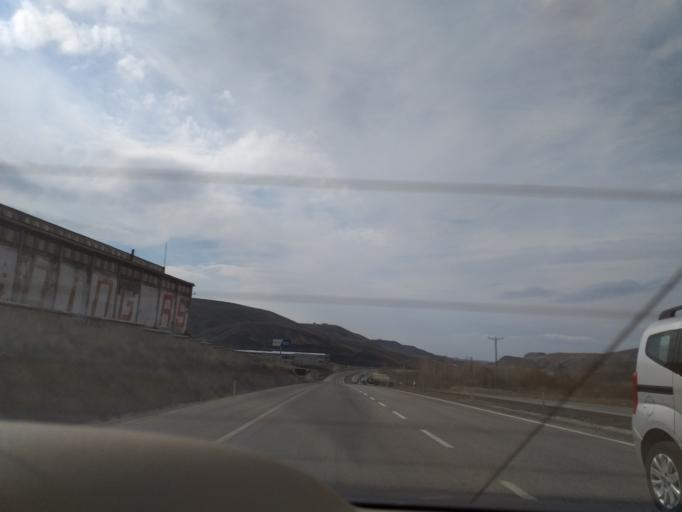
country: TR
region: Yozgat
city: Yozgat
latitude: 39.7904
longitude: 34.7579
